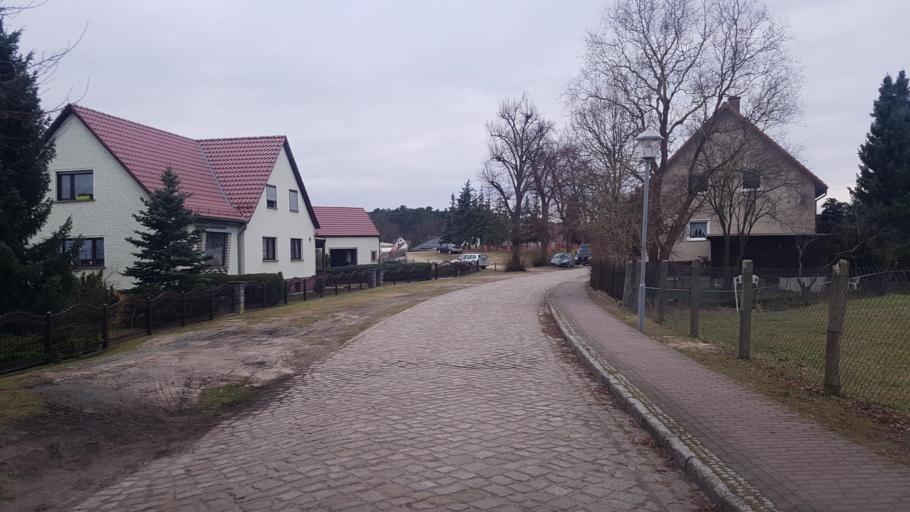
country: DE
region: Brandenburg
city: Halbe
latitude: 52.0673
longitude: 13.6951
